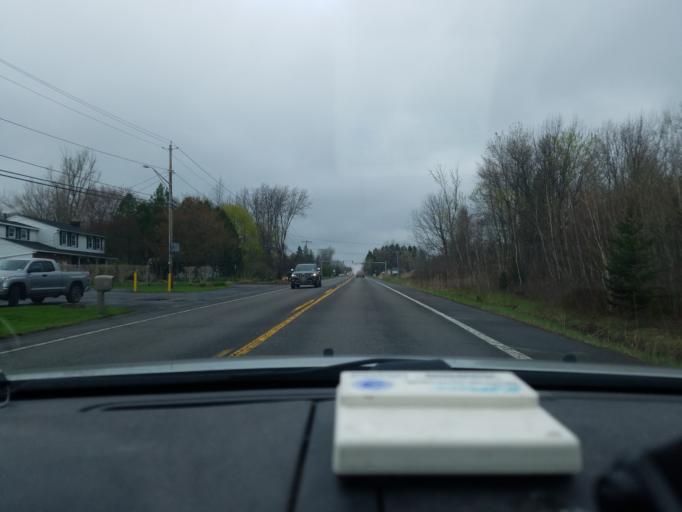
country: US
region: New York
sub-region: Onondaga County
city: North Syracuse
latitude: 43.1520
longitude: -76.1074
